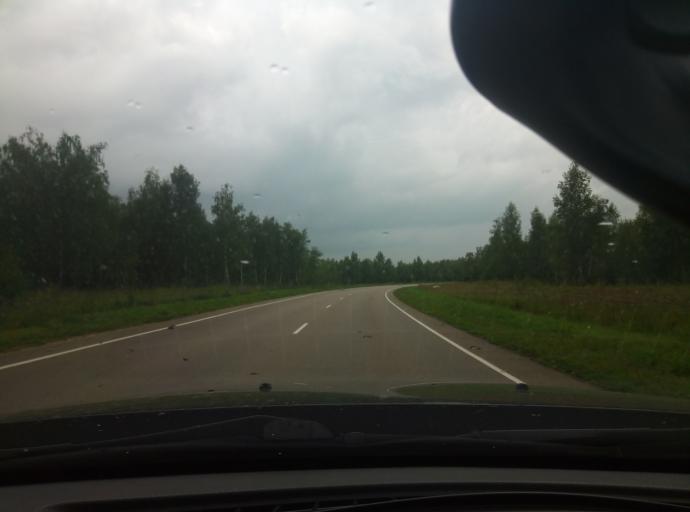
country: RU
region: Tula
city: Lomintsevskiy
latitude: 53.9383
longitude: 37.6176
